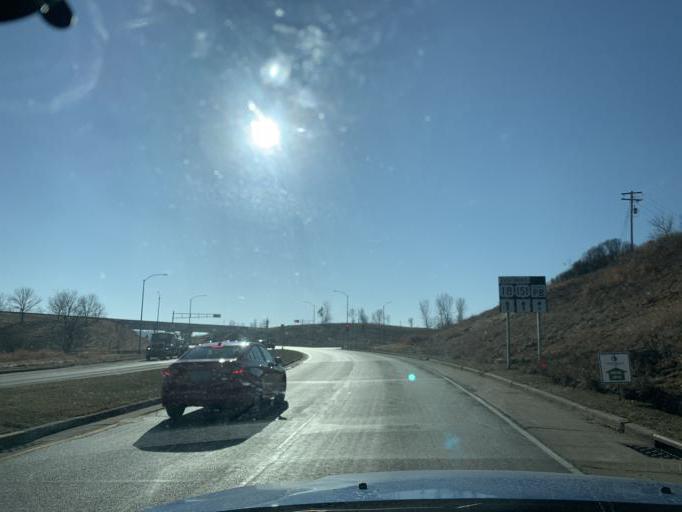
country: US
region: Wisconsin
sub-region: Dane County
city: Verona
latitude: 42.9775
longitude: -89.5141
